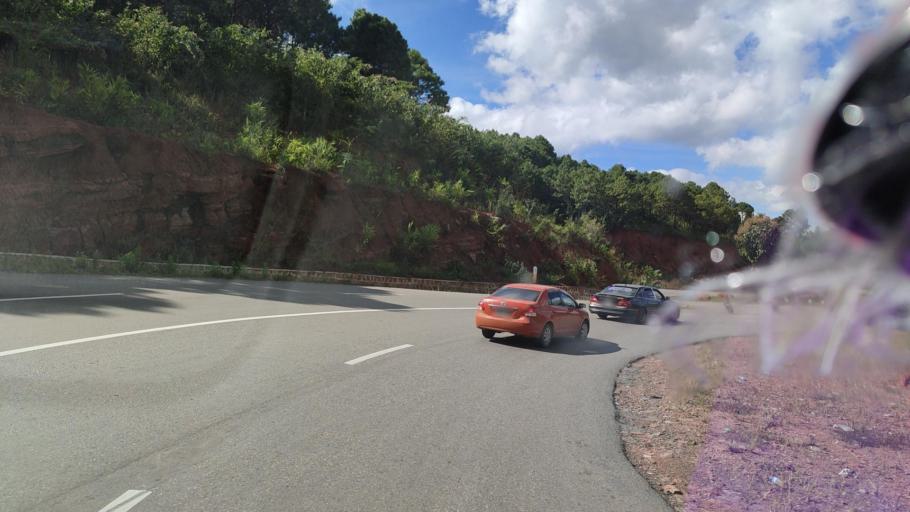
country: MM
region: Mandalay
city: Yamethin
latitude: 20.6511
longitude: 96.5510
